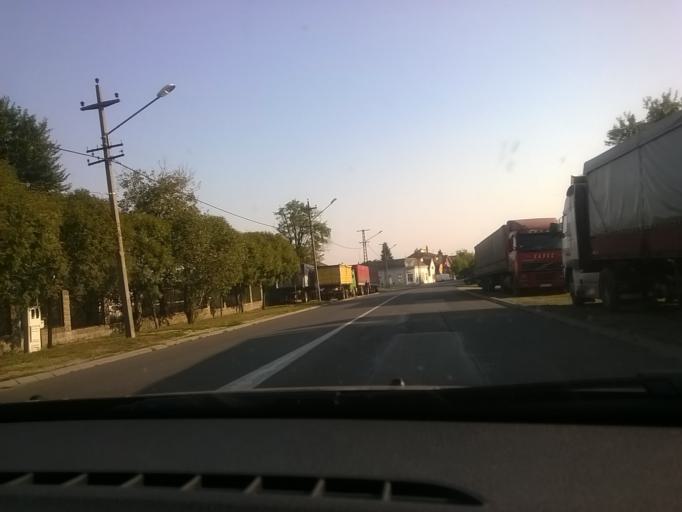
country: RS
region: Autonomna Pokrajina Vojvodina
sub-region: Juznobanatski Okrug
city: Vrsac
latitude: 45.1106
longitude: 21.2836
